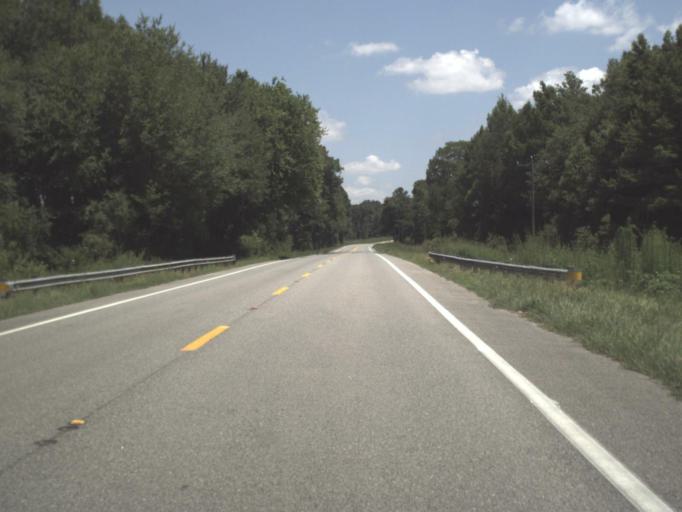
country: US
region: Florida
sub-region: Jefferson County
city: Monticello
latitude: 30.5541
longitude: -83.6365
